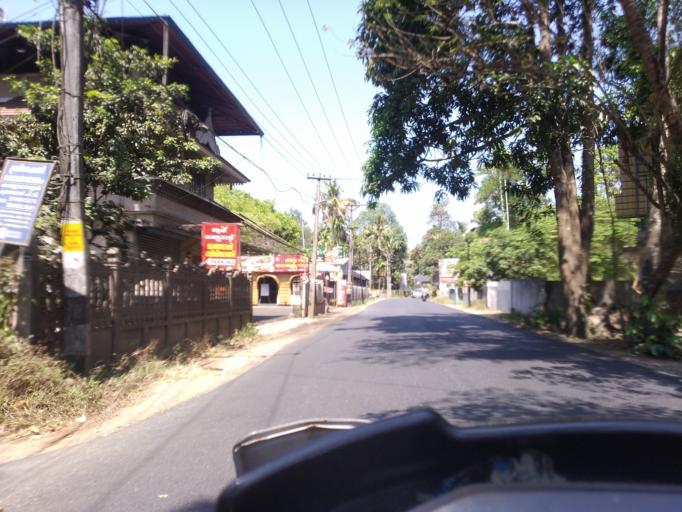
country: IN
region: Kerala
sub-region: Thrissur District
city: Kodungallur
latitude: 10.1630
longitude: 76.2142
